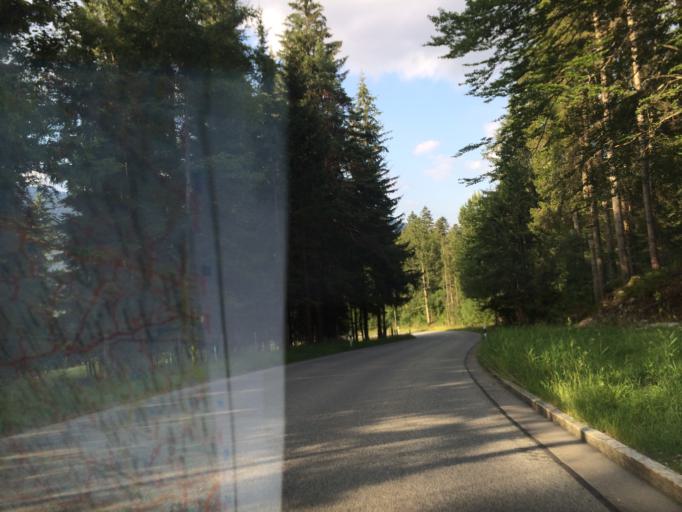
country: DE
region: Bavaria
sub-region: Upper Bavaria
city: Grainau
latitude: 47.4635
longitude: 11.0055
